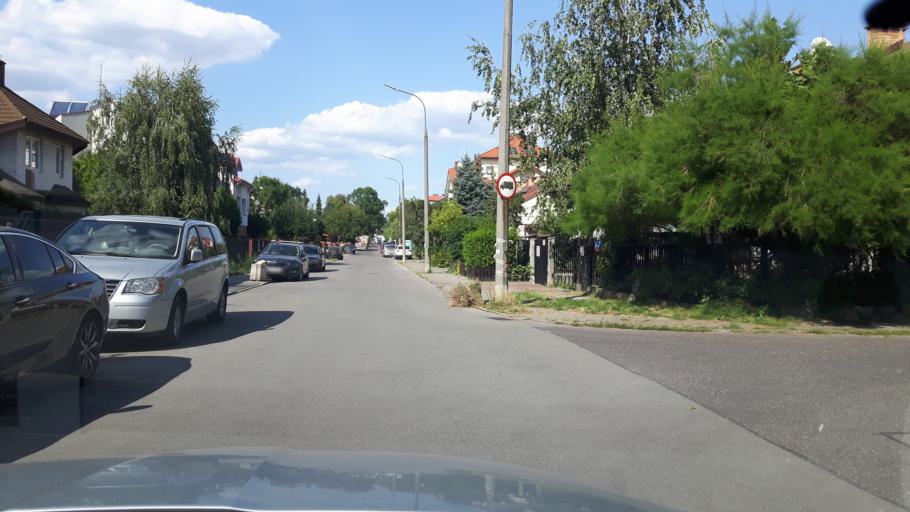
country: PL
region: Masovian Voivodeship
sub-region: Warszawa
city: Wlochy
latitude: 52.2010
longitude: 20.9200
